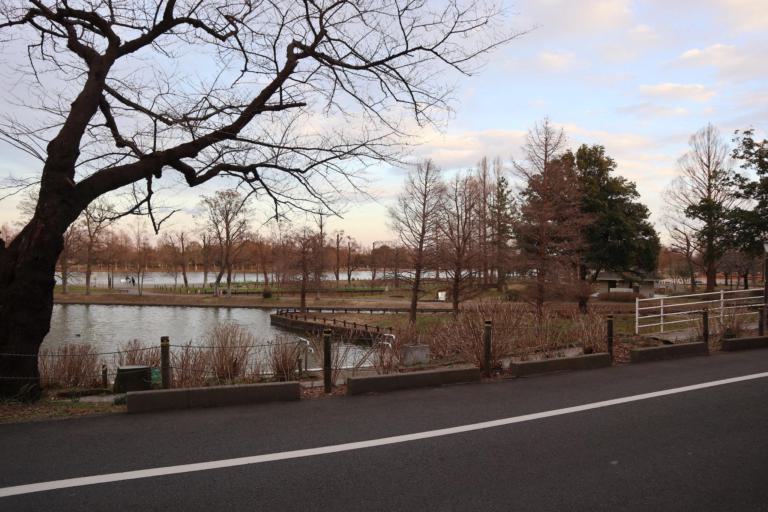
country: JP
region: Chiba
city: Matsudo
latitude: 35.7831
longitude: 139.8697
